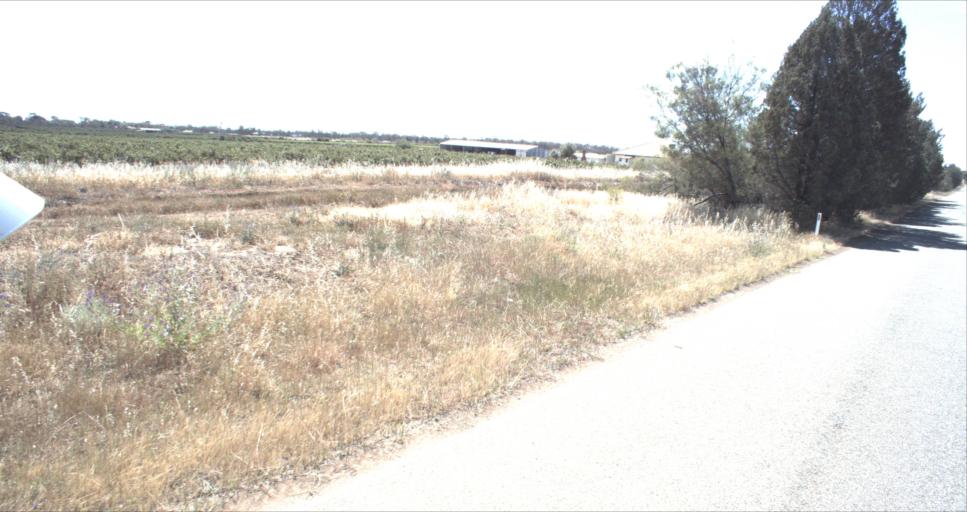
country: AU
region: New South Wales
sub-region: Leeton
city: Leeton
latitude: -34.5944
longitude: 146.4402
